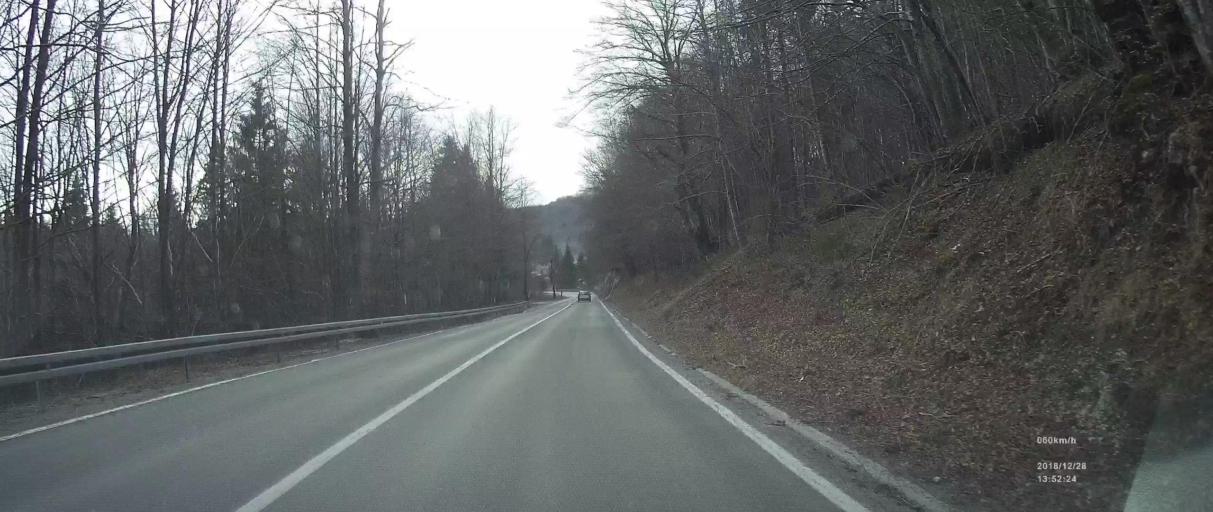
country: HR
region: Primorsko-Goranska
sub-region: Grad Delnice
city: Delnice
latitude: 45.3907
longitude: 14.8471
